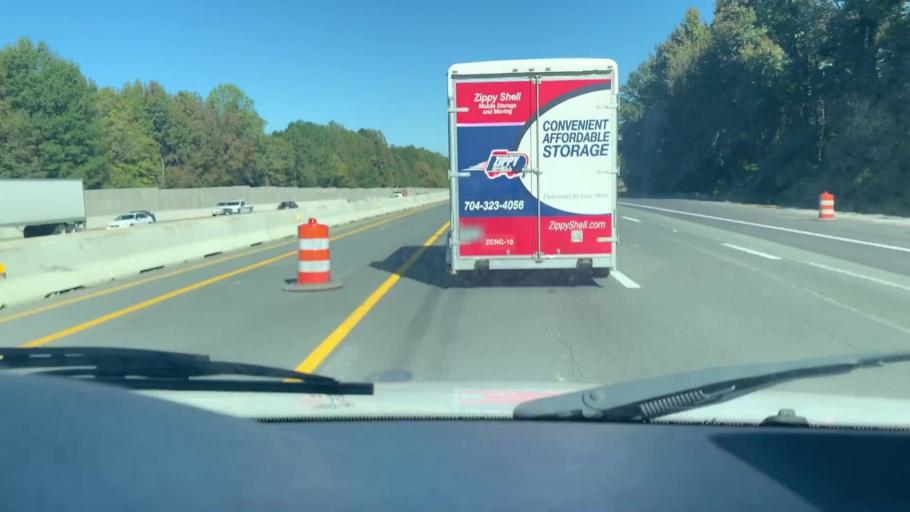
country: US
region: North Carolina
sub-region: Mecklenburg County
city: Huntersville
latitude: 35.3258
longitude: -80.8479
